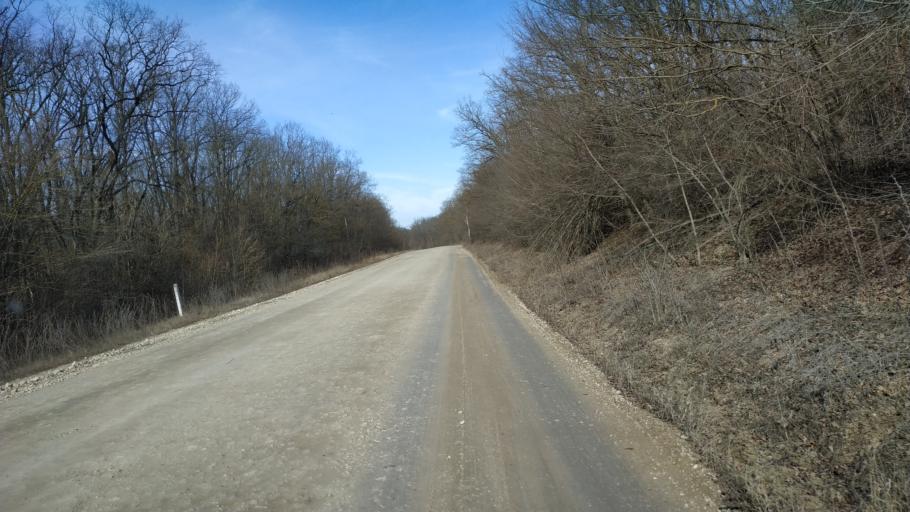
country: MD
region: Straseni
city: Straseni
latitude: 47.0368
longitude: 28.6136
